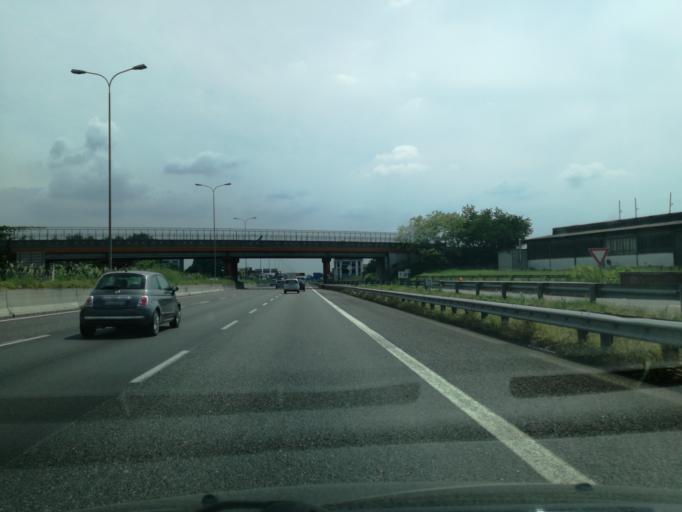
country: IT
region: Lombardy
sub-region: Provincia di Monza e Brianza
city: Verano Brianza
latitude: 45.6784
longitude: 9.2179
